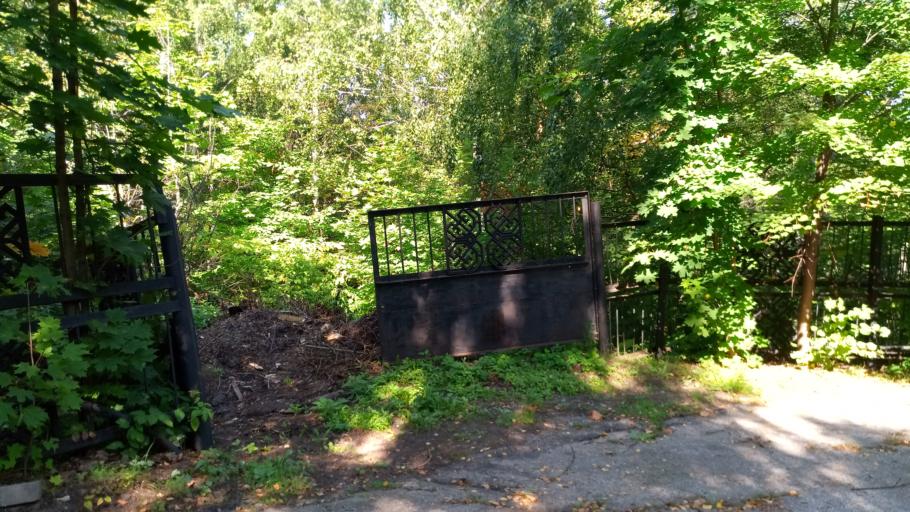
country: RU
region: Chuvashia
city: Ishley
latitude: 56.1278
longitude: 47.0385
